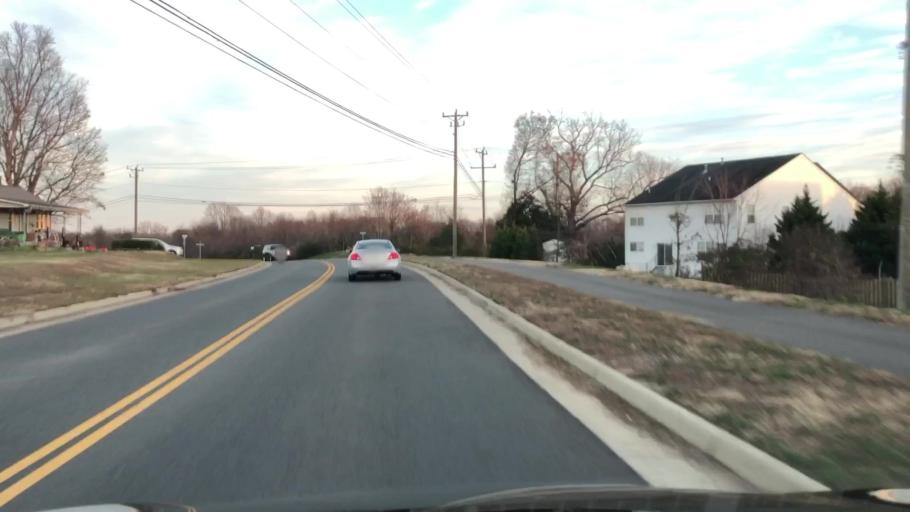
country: US
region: Virginia
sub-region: Stafford County
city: Falmouth
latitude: 38.3709
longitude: -77.4991
